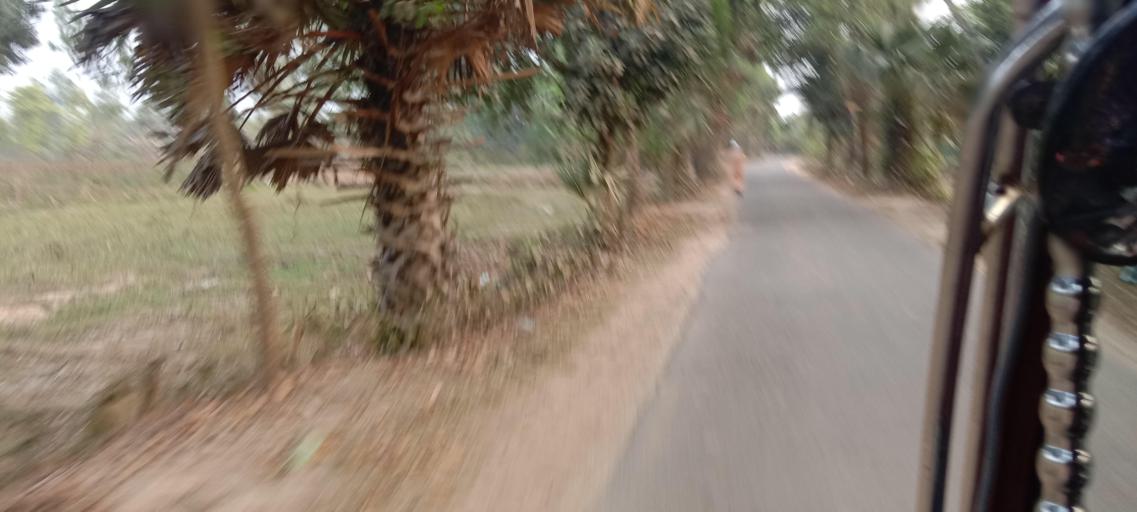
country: BD
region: Dhaka
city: Sakhipur
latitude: 24.4340
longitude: 90.2629
